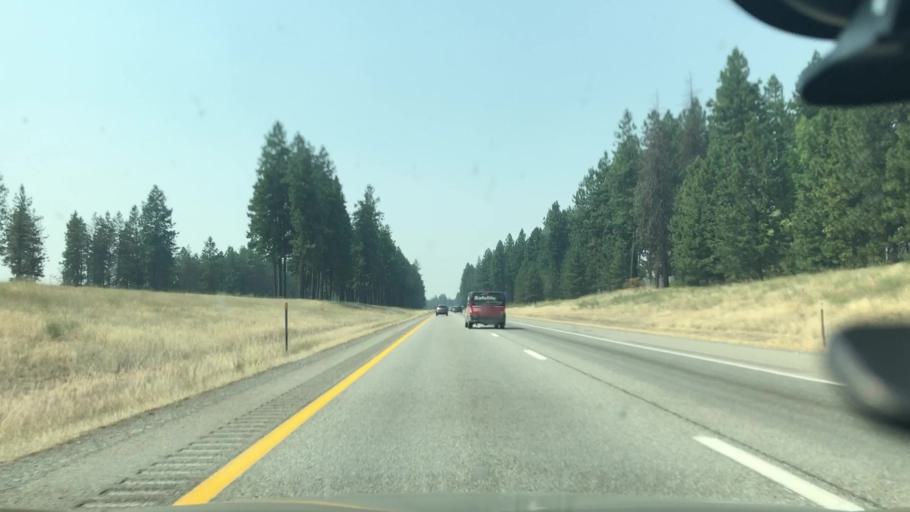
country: US
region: Idaho
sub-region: Kootenai County
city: Coeur d'Alene
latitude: 47.7054
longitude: -116.8391
